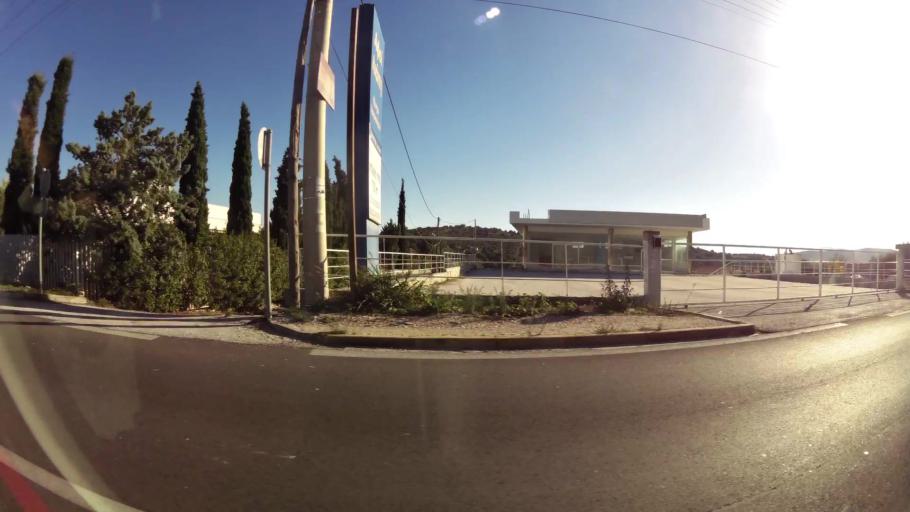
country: GR
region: Attica
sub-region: Nomarchia Anatolikis Attikis
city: Pikermi
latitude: 37.9980
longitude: 23.9299
